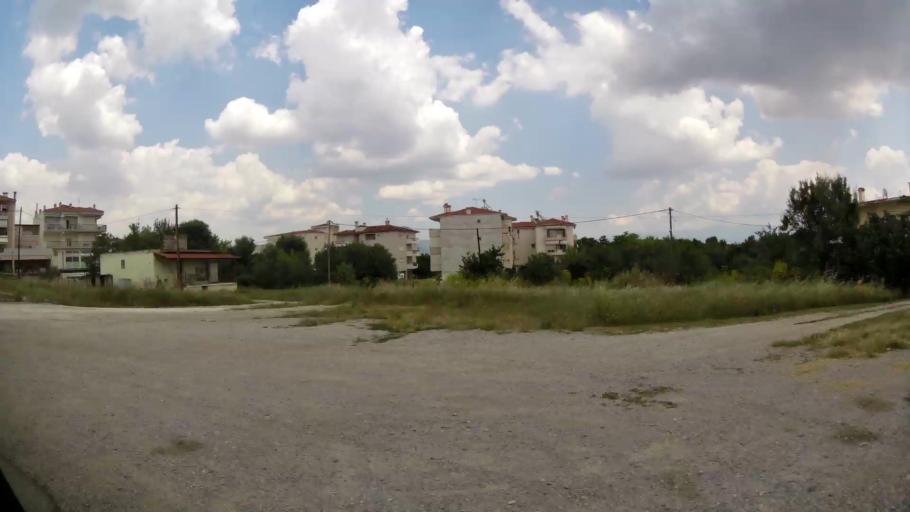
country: GR
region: West Macedonia
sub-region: Nomos Kozanis
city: Kozani
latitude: 40.2987
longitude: 21.8022
